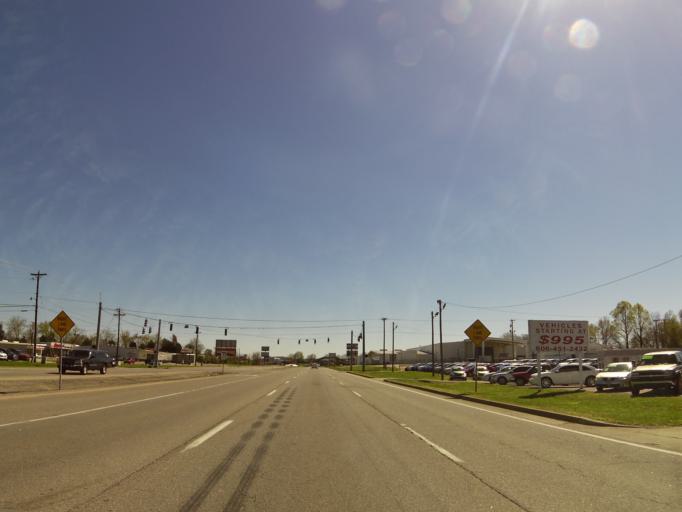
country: US
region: Kentucky
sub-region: Pulaski County
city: Somerset
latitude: 37.0219
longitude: -84.6271
